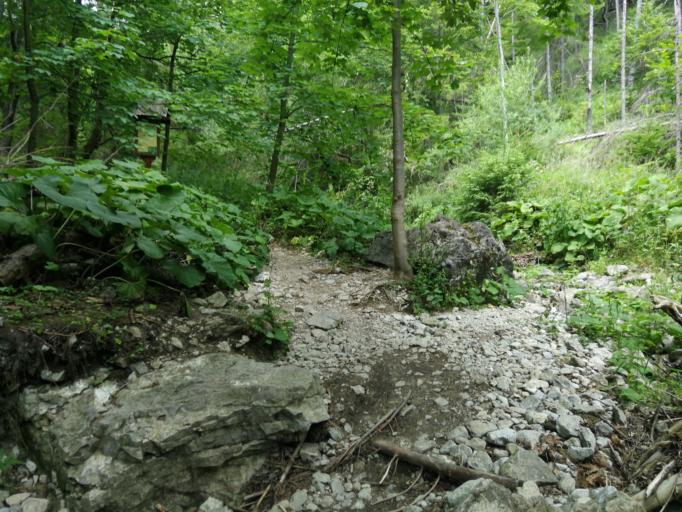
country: SK
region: Zilinsky
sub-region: Okres Liptovsky Mikulas
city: Liptovsky Mikulas
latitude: 49.1618
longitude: 19.4905
